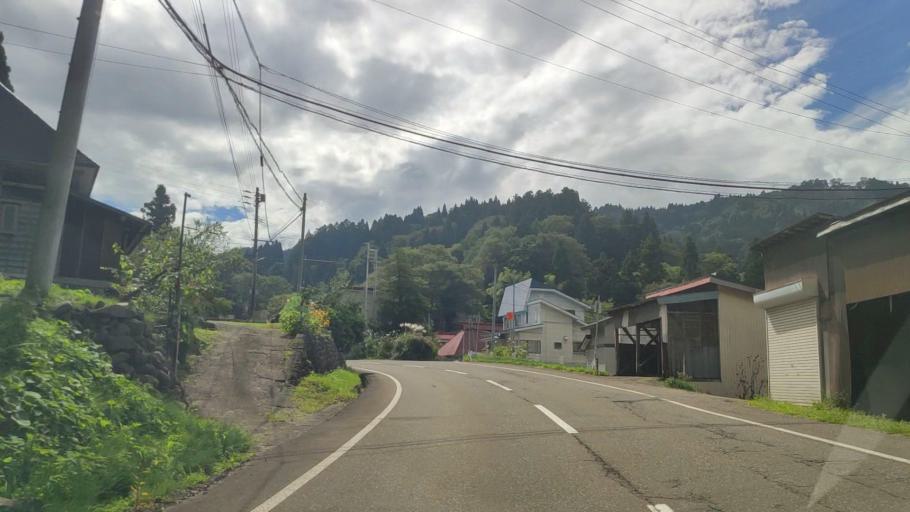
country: JP
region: Niigata
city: Arai
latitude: 36.9295
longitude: 138.2983
